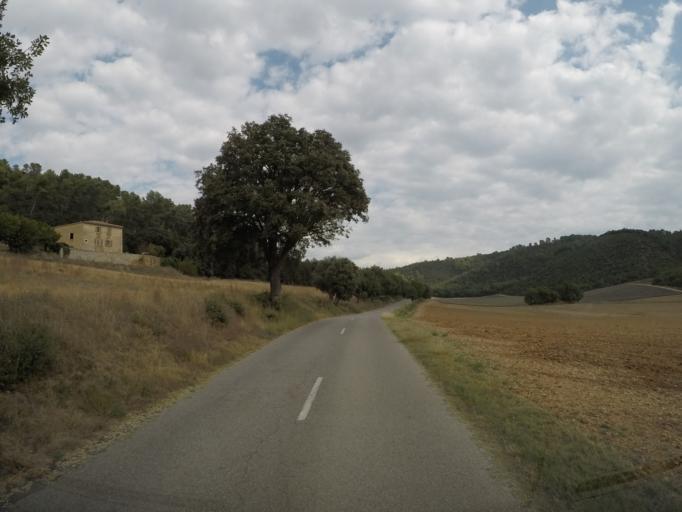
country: FR
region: Provence-Alpes-Cote d'Azur
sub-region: Departement des Alpes-de-Haute-Provence
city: Greoux-les-Bains
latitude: 43.7919
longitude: 5.9225
